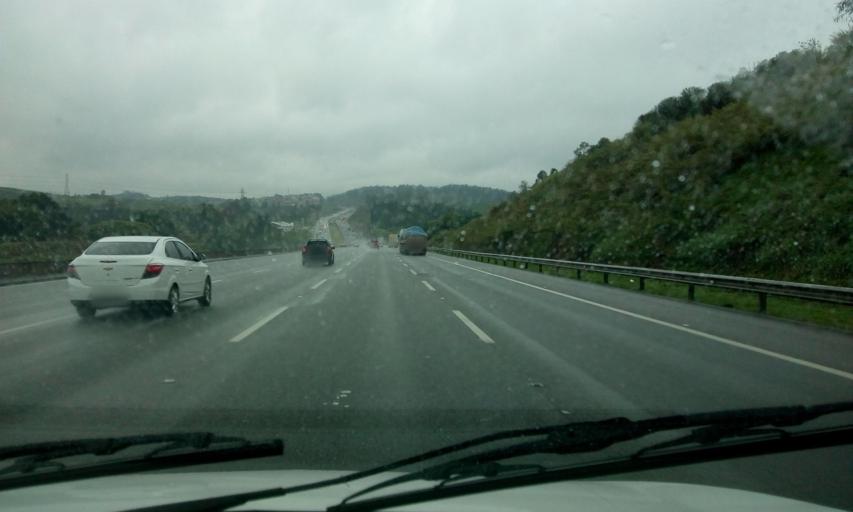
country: BR
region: Sao Paulo
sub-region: Caieiras
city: Caieiras
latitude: -23.3854
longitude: -46.7694
